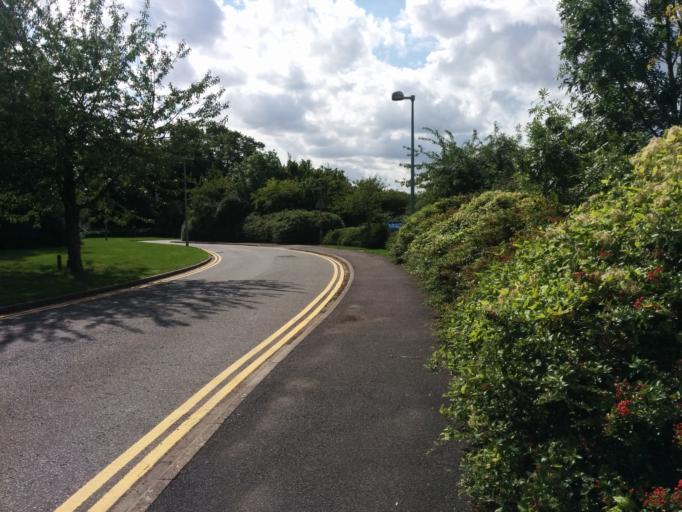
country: GB
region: England
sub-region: Cambridgeshire
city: Cambridge
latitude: 52.2068
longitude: 0.0988
